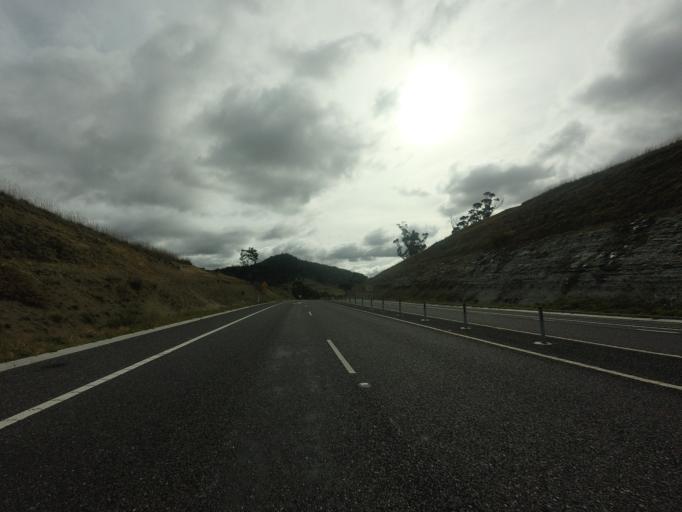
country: AU
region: Tasmania
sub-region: Brighton
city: Bridgewater
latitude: -42.5705
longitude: 147.2117
